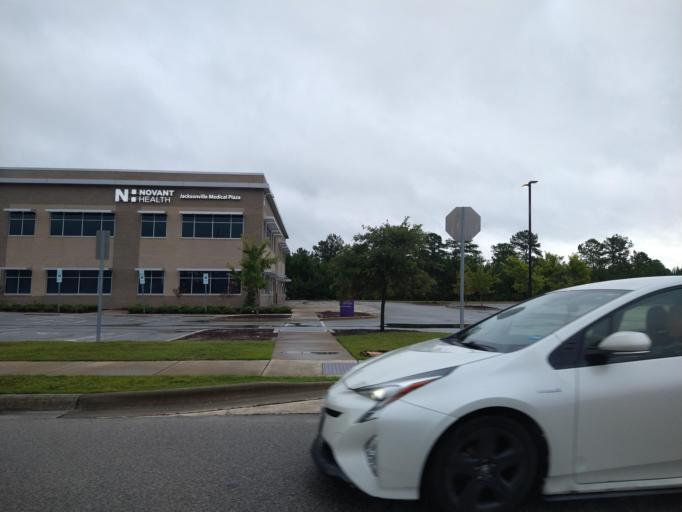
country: US
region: North Carolina
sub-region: Onslow County
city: Pumpkin Center
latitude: 34.7986
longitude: -77.4122
